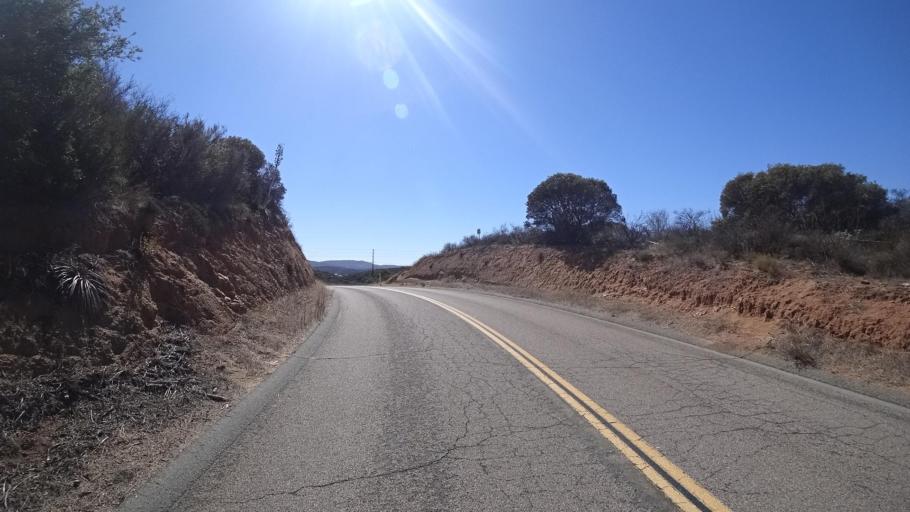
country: US
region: California
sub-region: San Diego County
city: Alpine
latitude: 32.8010
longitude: -116.7711
